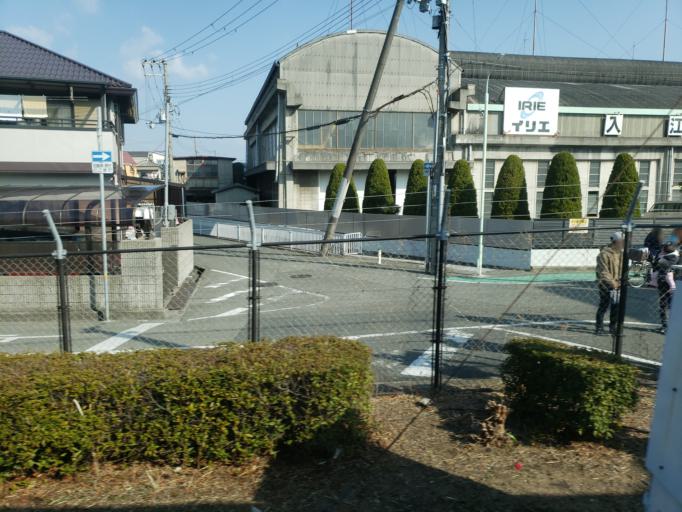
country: JP
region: Hyogo
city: Amagasaki
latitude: 34.7362
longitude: 135.4094
